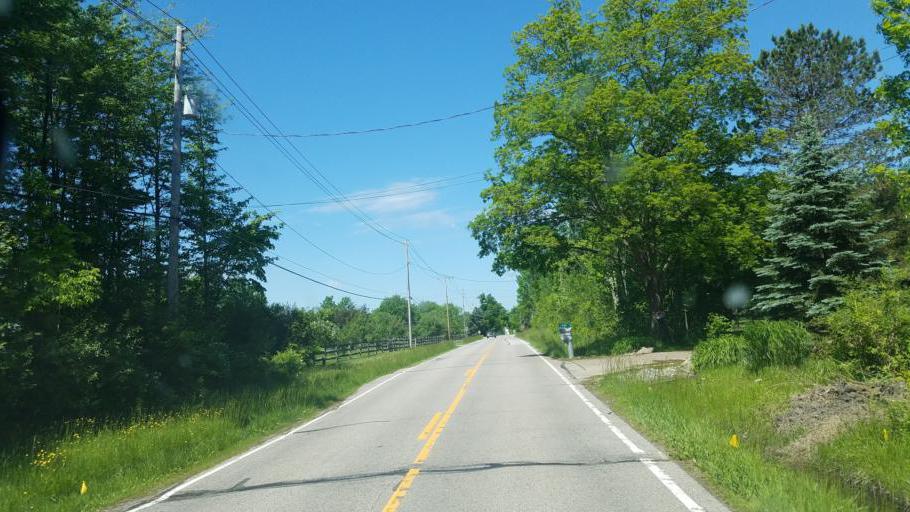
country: US
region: Ohio
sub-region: Geauga County
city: Bainbridge
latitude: 41.3695
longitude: -81.3065
